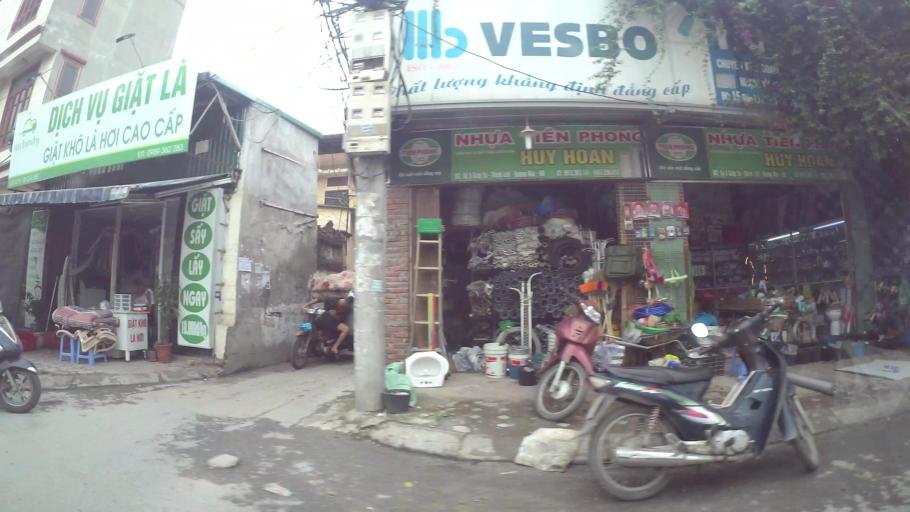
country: VN
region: Ha Noi
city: Van Dien
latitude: 20.9768
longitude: 105.8487
